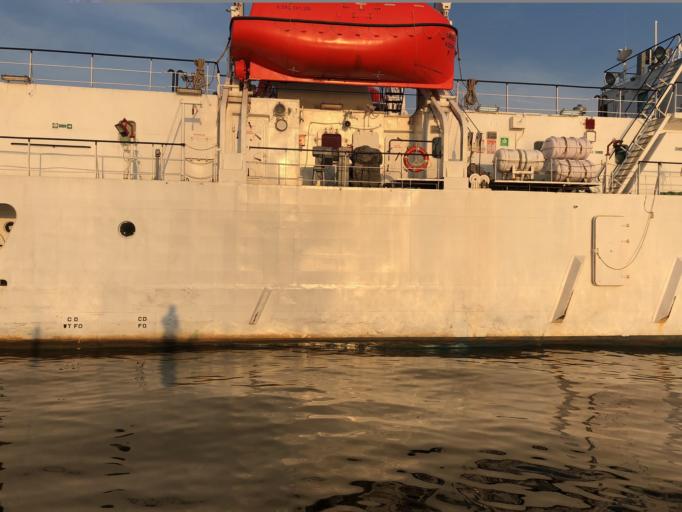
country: IN
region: Karnataka
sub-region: Dakshina Kannada
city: Ullal
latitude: 12.8609
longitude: 74.8315
